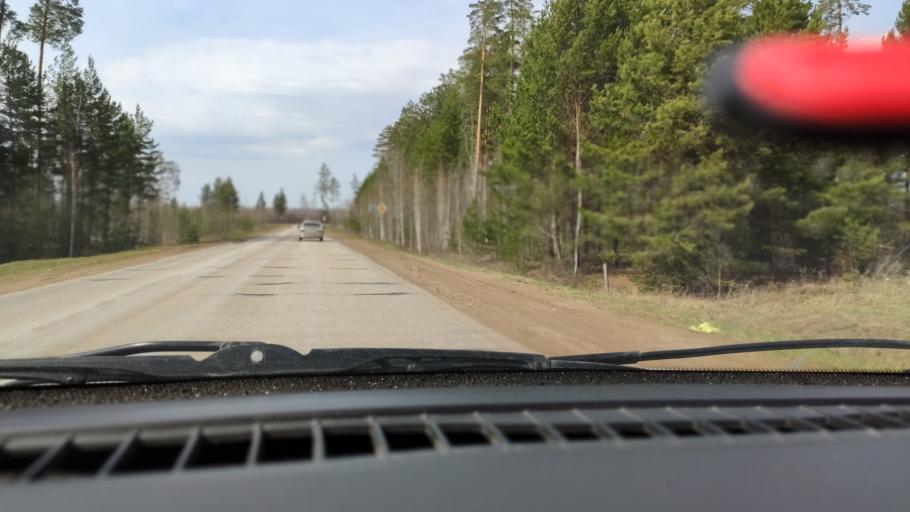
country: RU
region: Bashkortostan
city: Dyurtyuli
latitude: 55.5348
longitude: 54.8638
